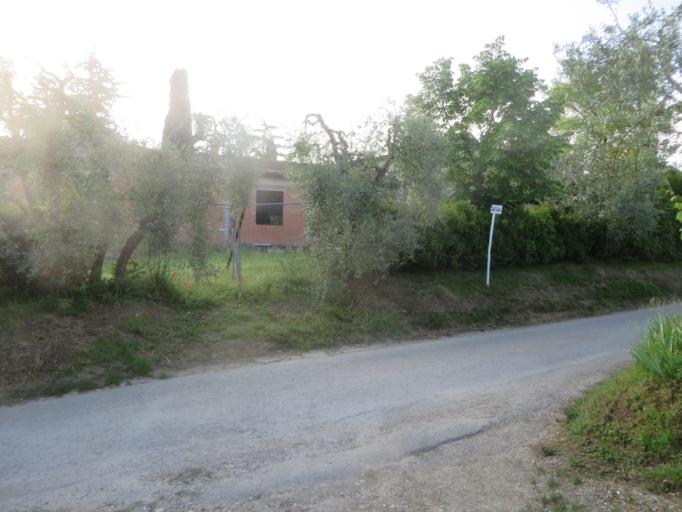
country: IT
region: Tuscany
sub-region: Province of Florence
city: Bagno a Ripoli
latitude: 43.7447
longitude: 11.3257
